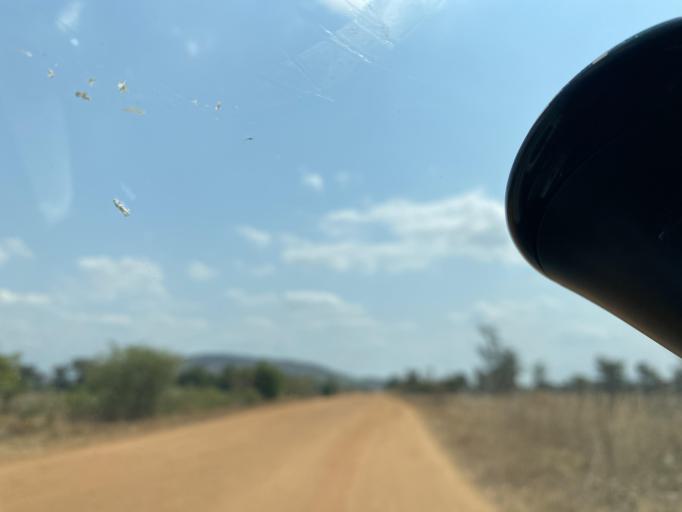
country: ZM
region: Lusaka
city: Chongwe
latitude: -15.5912
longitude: 28.7590
